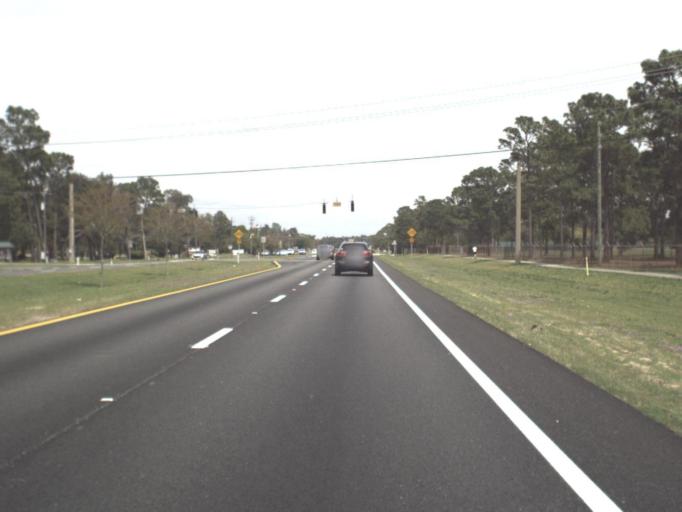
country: US
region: Florida
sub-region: Okaloosa County
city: Wright
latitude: 30.4658
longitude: -86.6169
